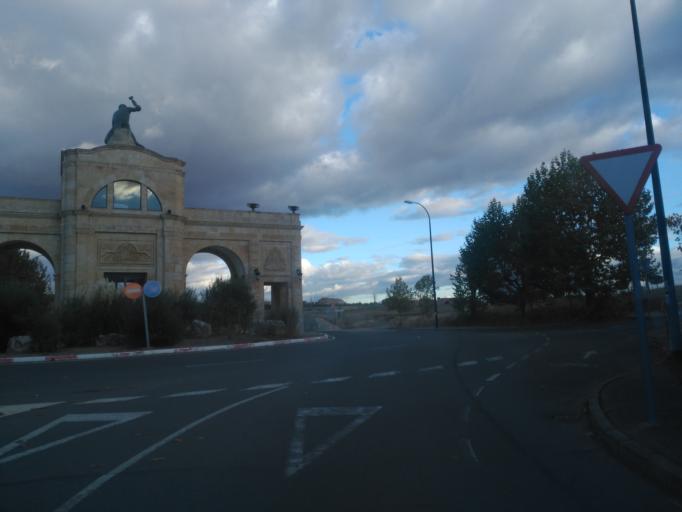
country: ES
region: Castille and Leon
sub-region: Provincia de Salamanca
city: Villamayor
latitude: 40.9811
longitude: -5.6958
